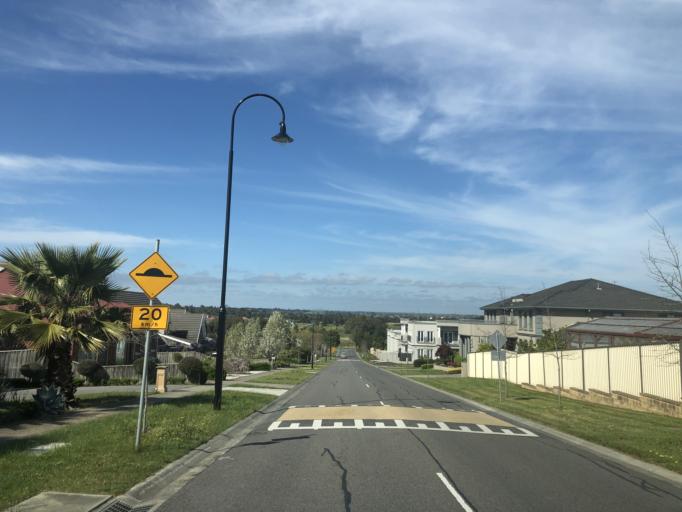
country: AU
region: Victoria
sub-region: Casey
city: Narre Warren North
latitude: -37.9924
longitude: 145.2918
